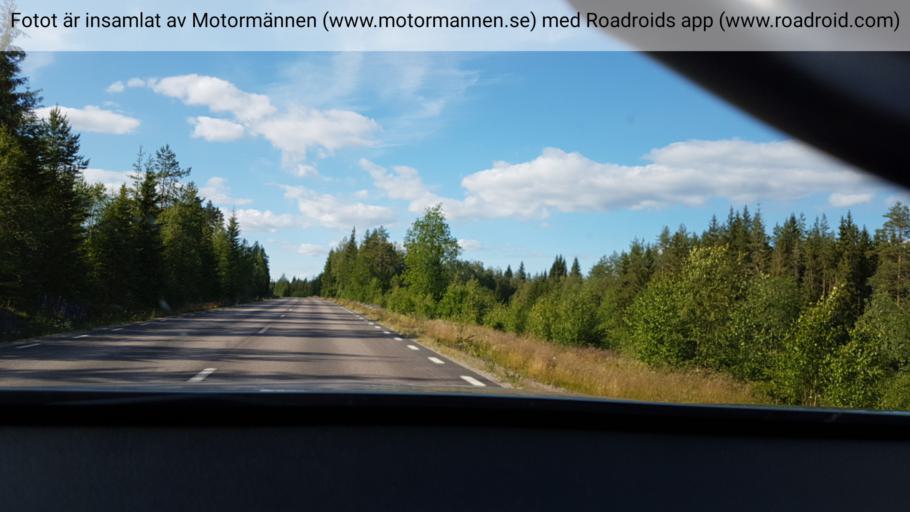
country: SE
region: Vaermland
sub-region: Filipstads Kommun
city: Lesjofors
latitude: 59.8771
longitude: 14.0086
